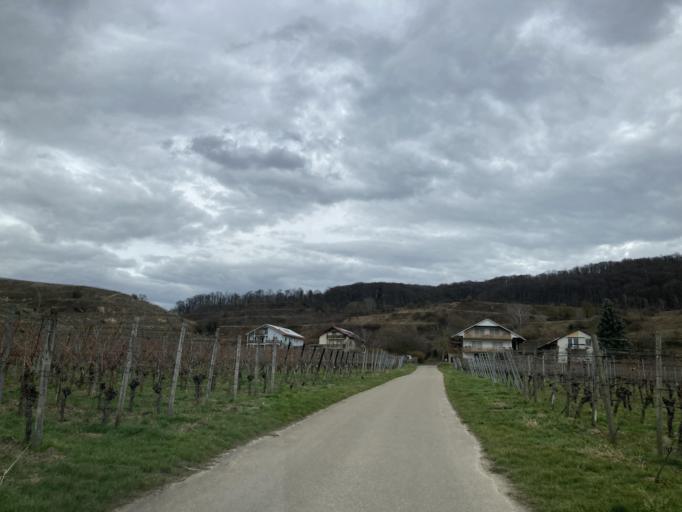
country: DE
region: Baden-Wuerttemberg
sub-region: Freiburg Region
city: Vogtsburg
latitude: 48.1065
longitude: 7.6330
